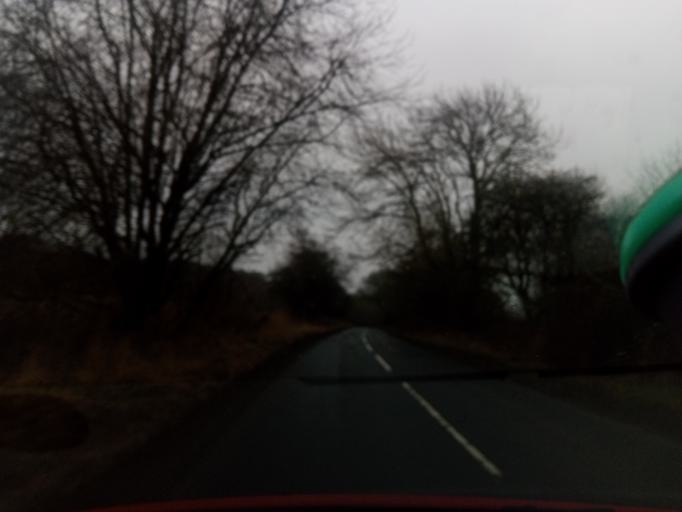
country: GB
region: England
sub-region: Northumberland
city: Rochester
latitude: 55.1560
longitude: -2.2950
